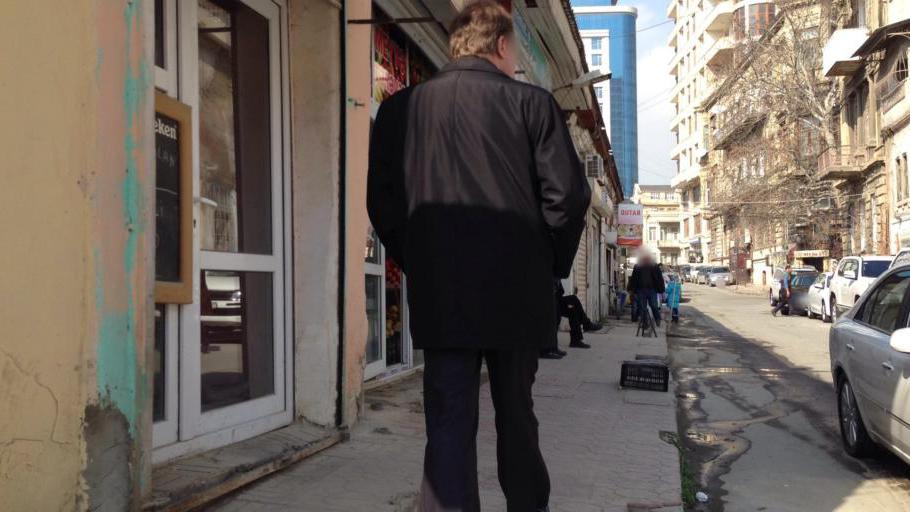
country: AZ
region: Baki
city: Badamdar
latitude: 40.3737
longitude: 49.8382
